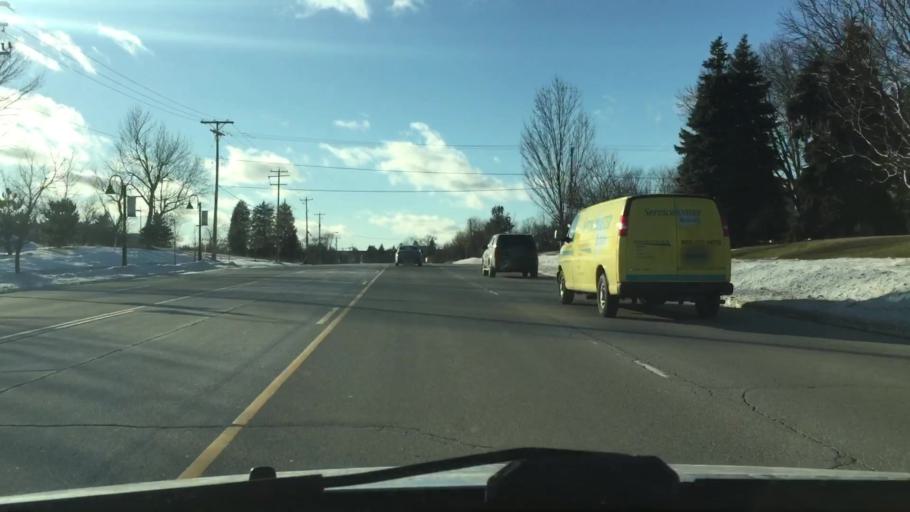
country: US
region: Wisconsin
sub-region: Waukesha County
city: New Berlin
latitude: 42.9883
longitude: -88.0725
